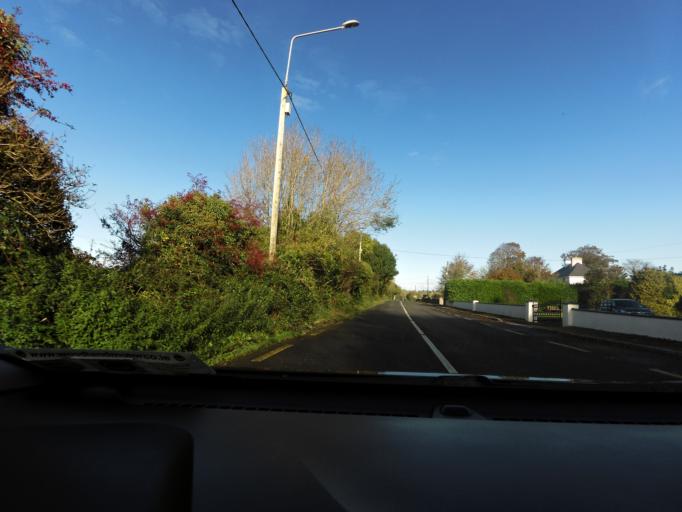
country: IE
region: Connaught
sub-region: Maigh Eo
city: Ballinrobe
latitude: 53.5252
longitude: -9.0922
